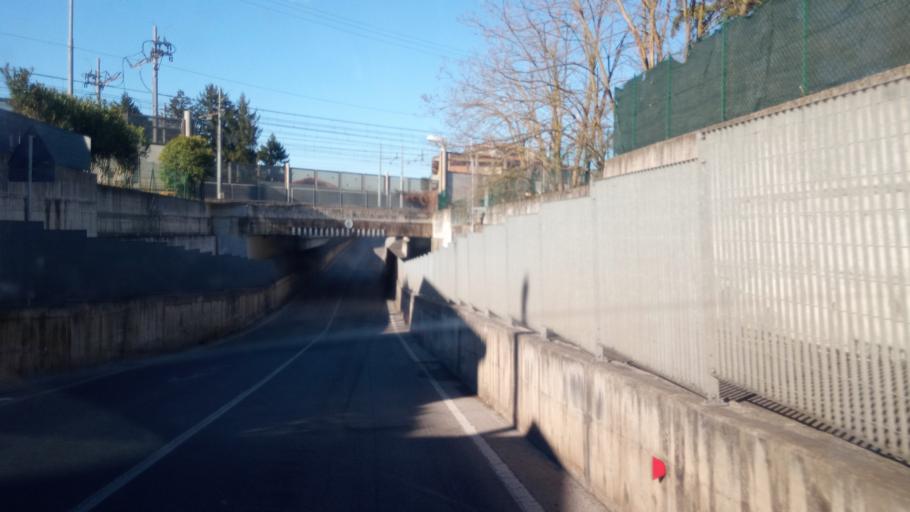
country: IT
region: Veneto
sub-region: Provincia di Padova
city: Padova
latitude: 45.4214
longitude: 11.9099
